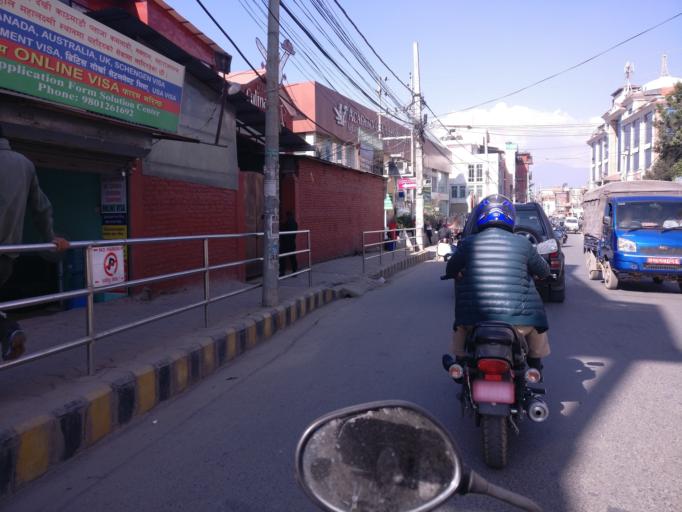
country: NP
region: Central Region
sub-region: Bagmati Zone
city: Patan
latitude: 27.6663
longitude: 85.3209
